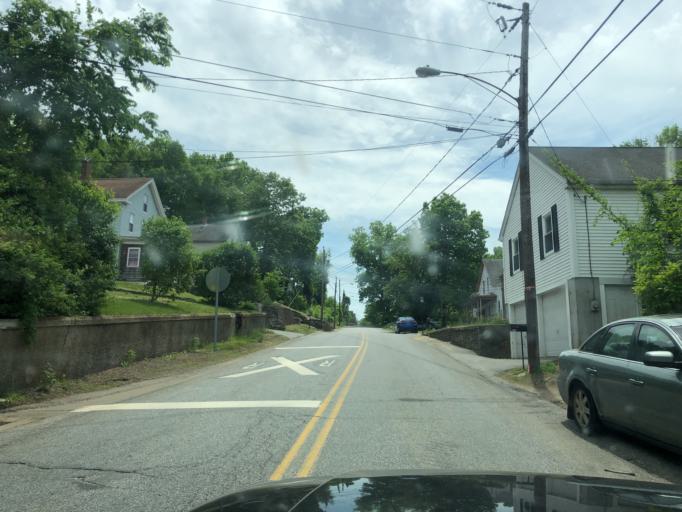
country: US
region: Connecticut
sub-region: Windham County
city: North Grosvenor Dale
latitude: 41.9870
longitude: -71.8947
